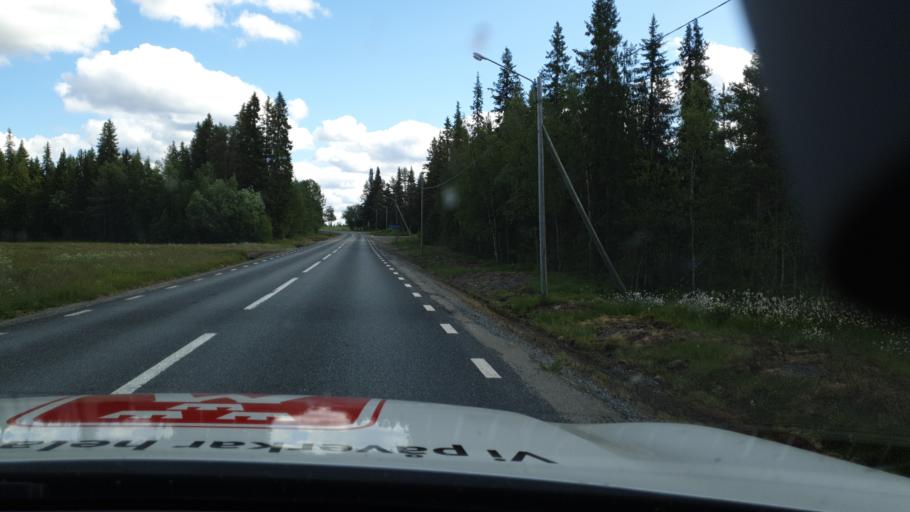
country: SE
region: Vaesterbotten
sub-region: Sorsele Kommun
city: Sorsele
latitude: 65.5575
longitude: 17.8427
